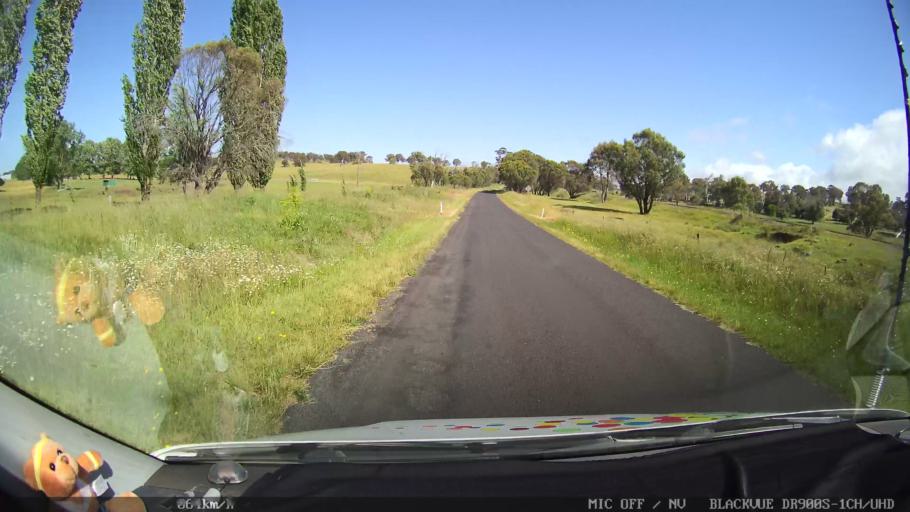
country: AU
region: New South Wales
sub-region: Guyra
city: Guyra
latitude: -30.0673
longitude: 151.6680
